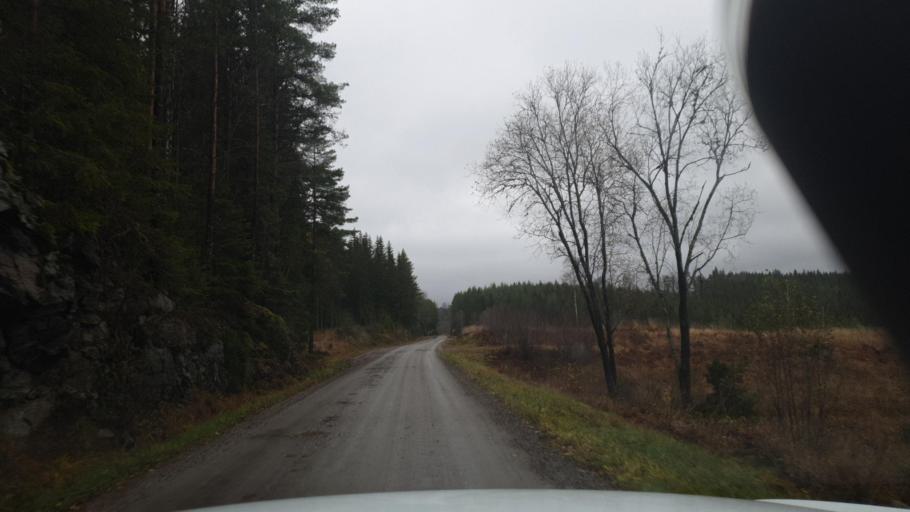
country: SE
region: Vaermland
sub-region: Eda Kommun
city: Charlottenberg
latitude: 60.0211
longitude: 12.5072
